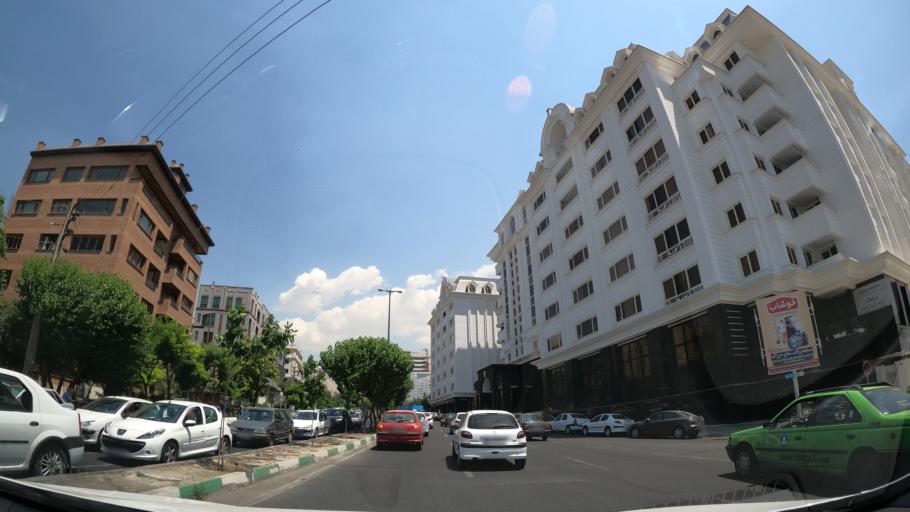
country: IR
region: Tehran
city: Tajrish
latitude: 35.7674
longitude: 51.3787
